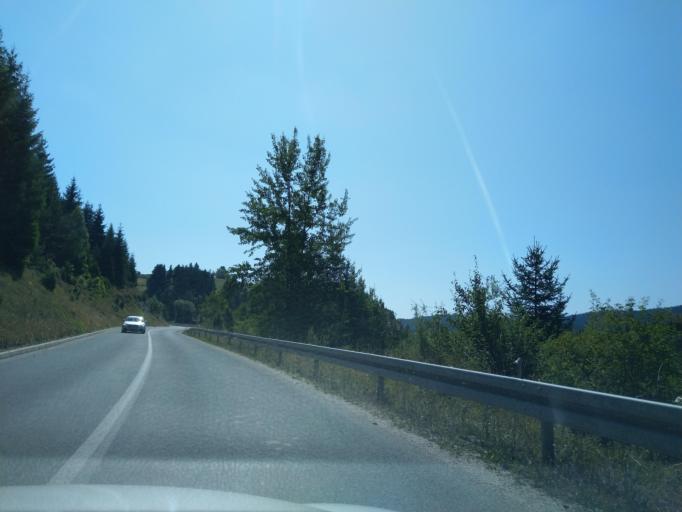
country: RS
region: Central Serbia
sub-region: Zlatiborski Okrug
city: Nova Varos
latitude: 43.4339
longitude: 19.8247
